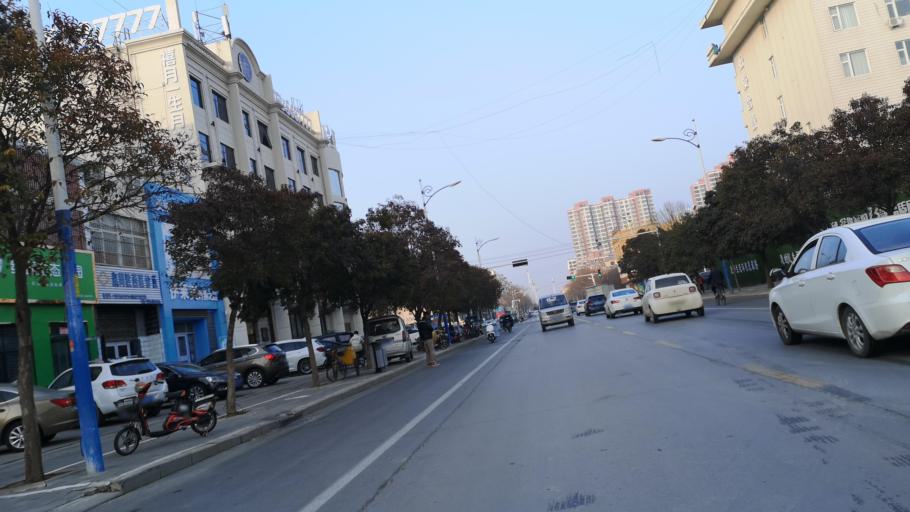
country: CN
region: Henan Sheng
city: Zhongyuanlu
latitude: 35.7689
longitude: 115.0636
